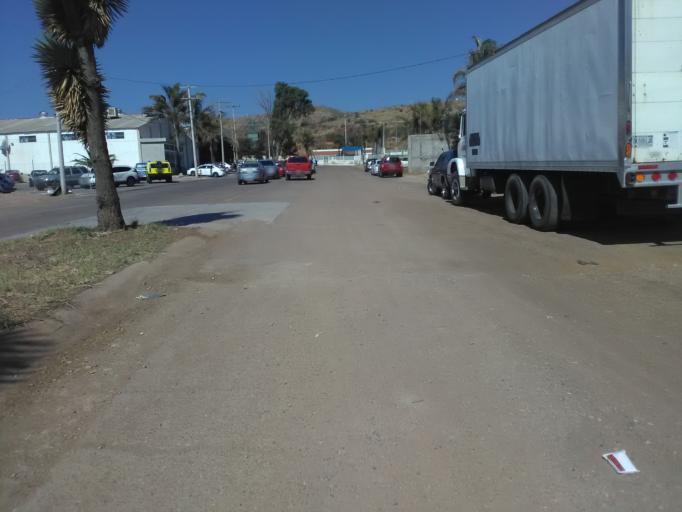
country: MX
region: Durango
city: Victoria de Durango
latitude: 24.0543
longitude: -104.6554
